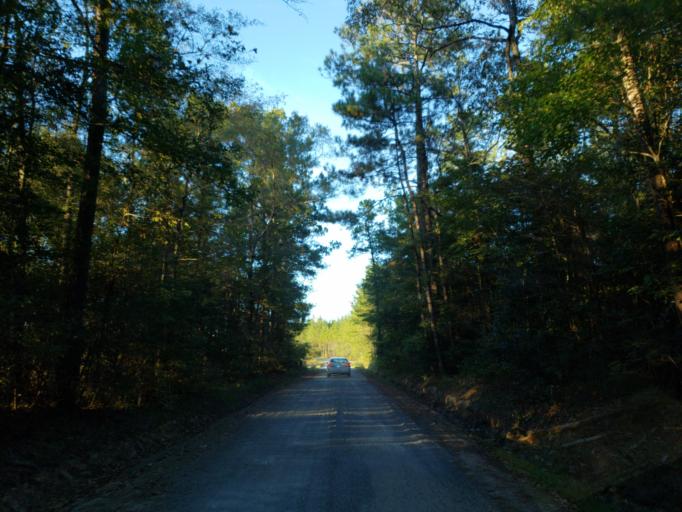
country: US
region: Mississippi
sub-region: Wayne County
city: Belmont
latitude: 31.4316
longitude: -88.5260
